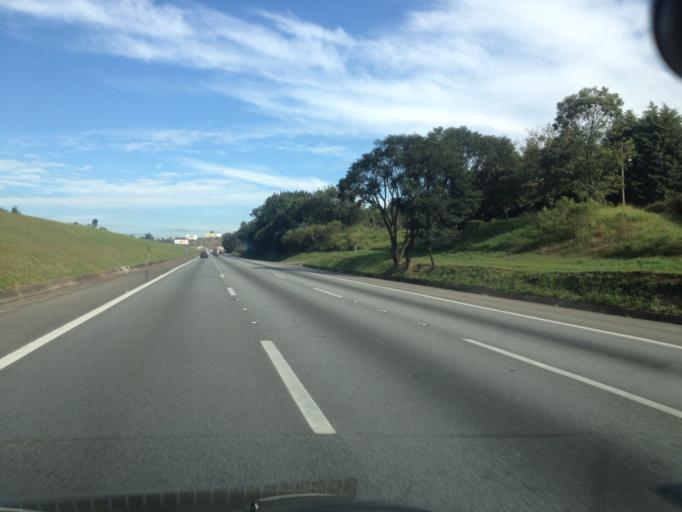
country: BR
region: Sao Paulo
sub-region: Mairinque
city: Mairinque
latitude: -23.4207
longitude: -47.2281
